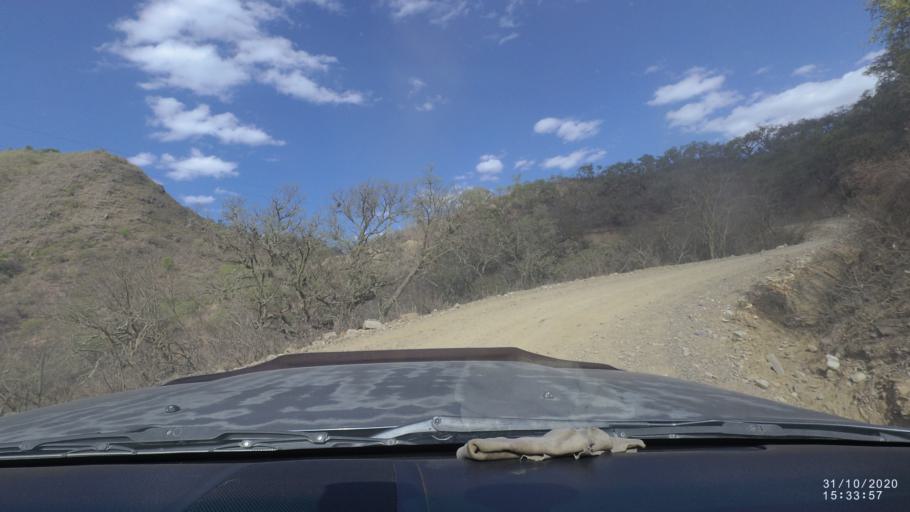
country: BO
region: Chuquisaca
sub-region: Provincia Zudanez
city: Mojocoya
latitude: -18.3426
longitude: -64.7559
